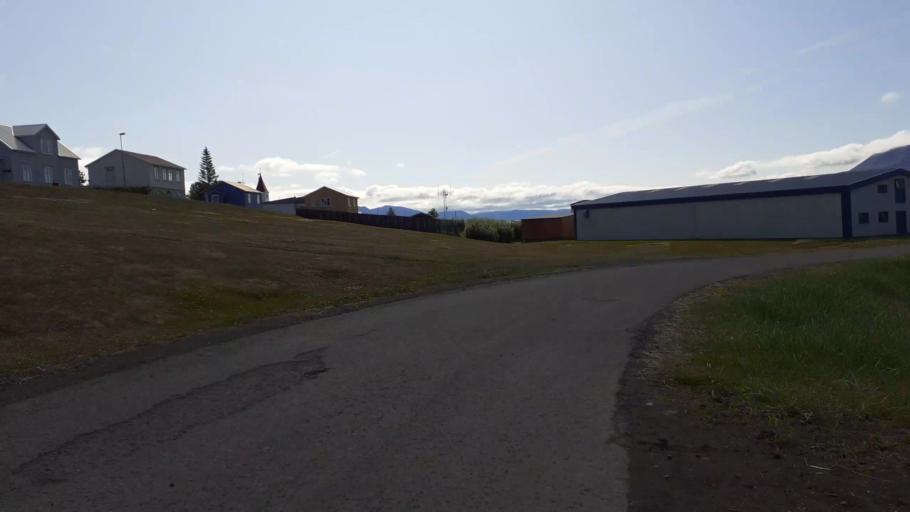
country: IS
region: Northeast
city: Dalvik
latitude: 65.9803
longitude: -18.3797
